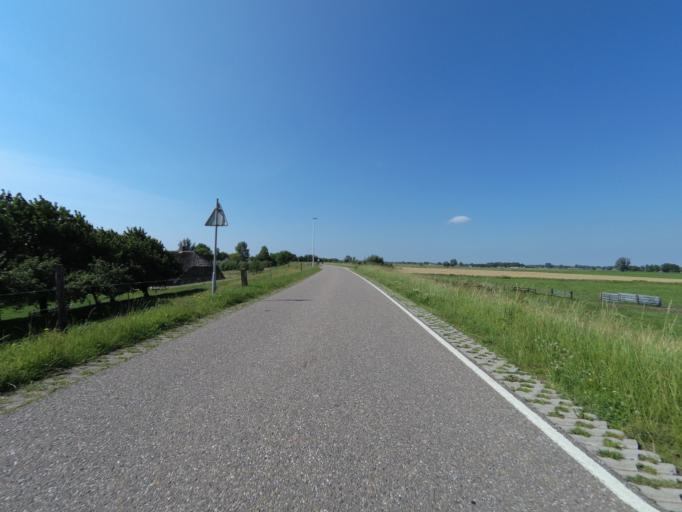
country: NL
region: Utrecht
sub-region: Gemeente IJsselstein
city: IJsselstein
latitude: 51.9731
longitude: 5.0479
